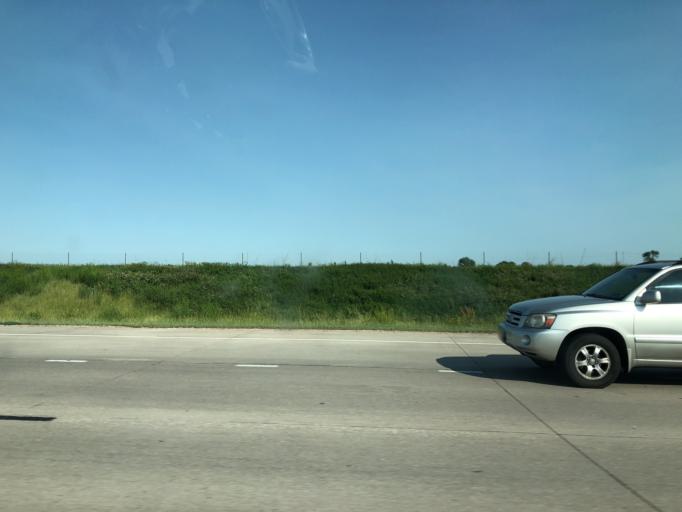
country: US
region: Nebraska
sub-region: Saunders County
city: Ashland
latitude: 40.9751
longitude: -96.3828
